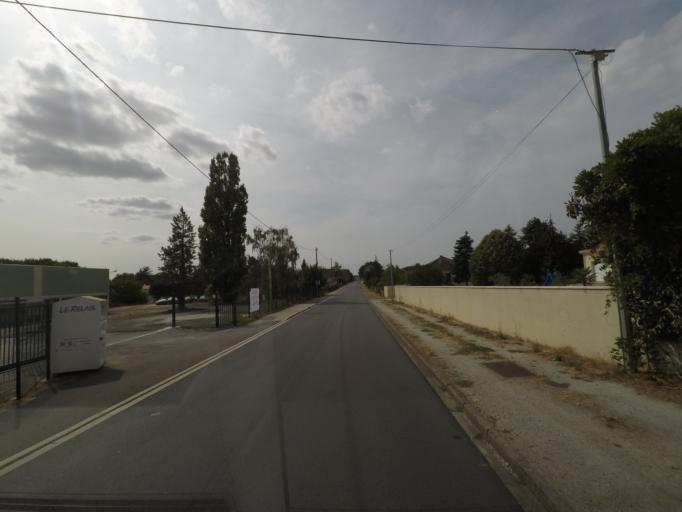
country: FR
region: Poitou-Charentes
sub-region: Departement de la Charente
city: Ruffec
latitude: 46.0262
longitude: 0.2149
